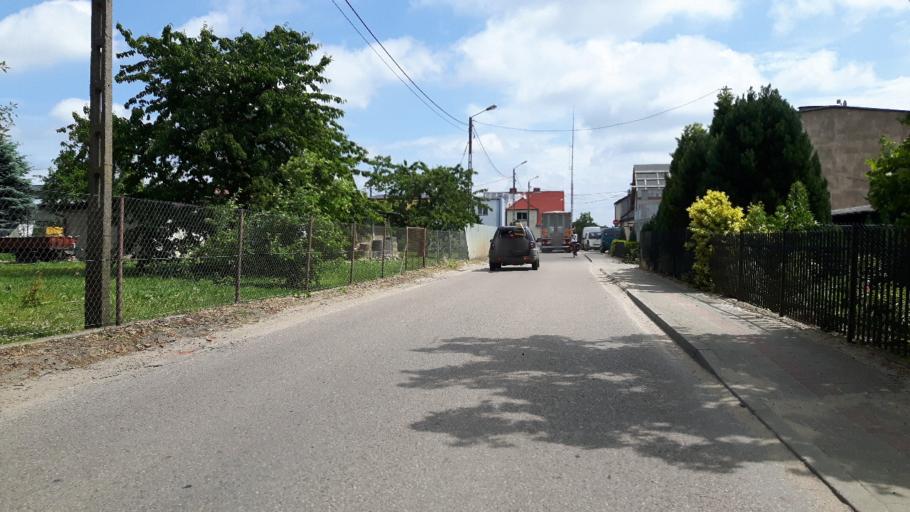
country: PL
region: Pomeranian Voivodeship
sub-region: Powiat wejherowski
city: Choczewo
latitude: 54.7415
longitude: 17.8901
